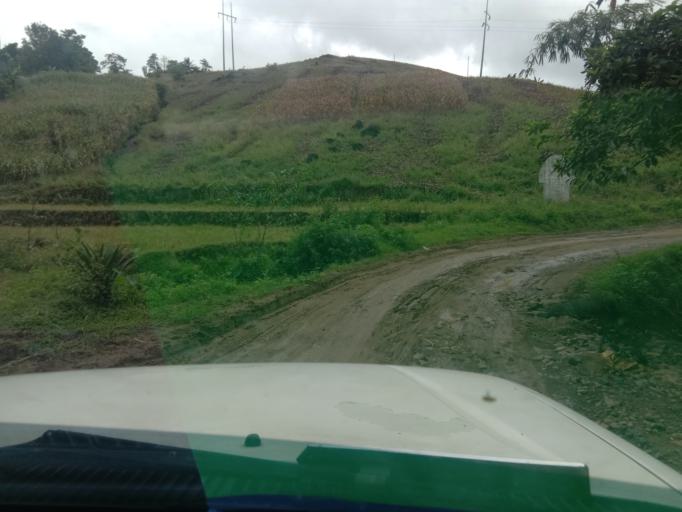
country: PH
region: Western Visayas
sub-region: Province of Capiz
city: Lantangan
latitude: 11.3714
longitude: 122.8854
